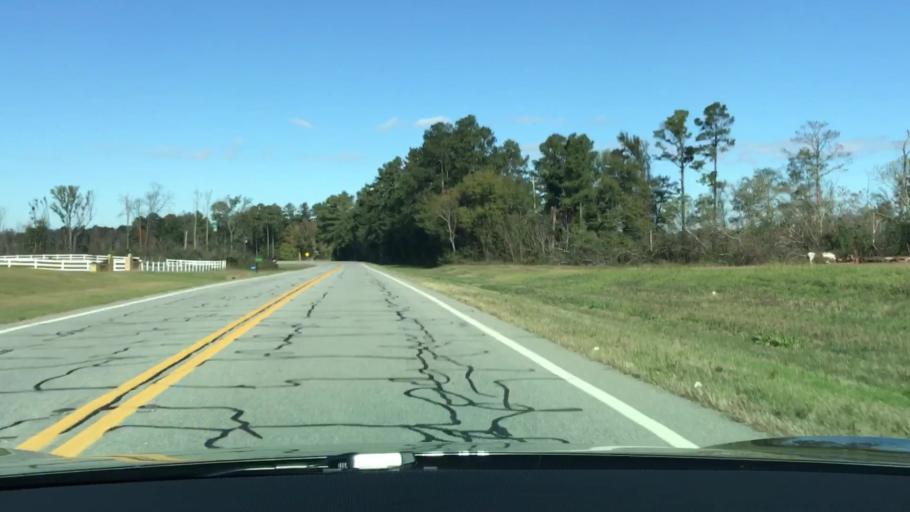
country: US
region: Georgia
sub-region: Warren County
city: Warrenton
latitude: 33.3717
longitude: -82.6018
